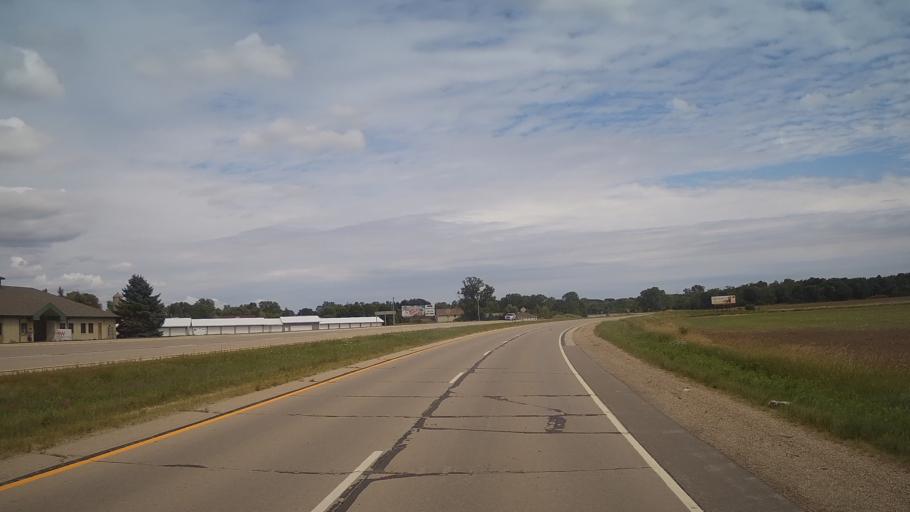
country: US
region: Wisconsin
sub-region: Winnebago County
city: Oshkosh
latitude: 44.0323
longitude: -88.6224
